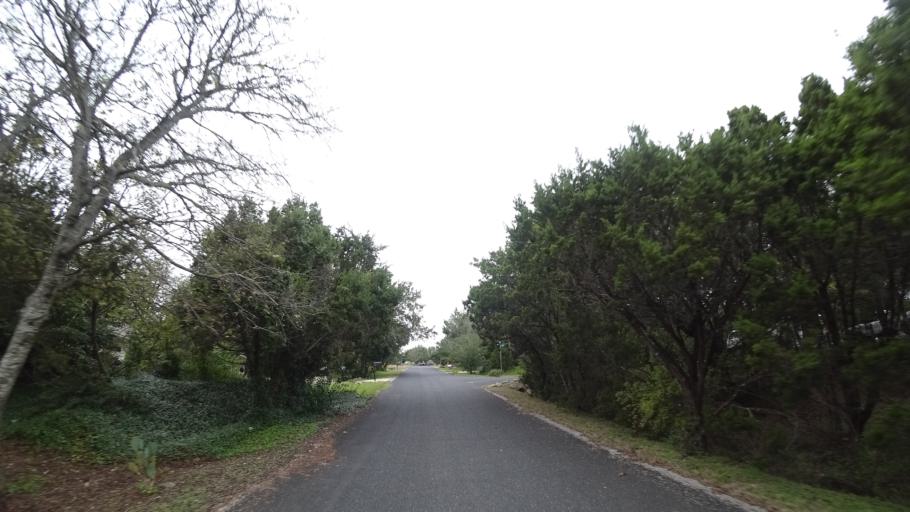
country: US
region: Texas
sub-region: Travis County
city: Barton Creek
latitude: 30.2402
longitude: -97.8891
